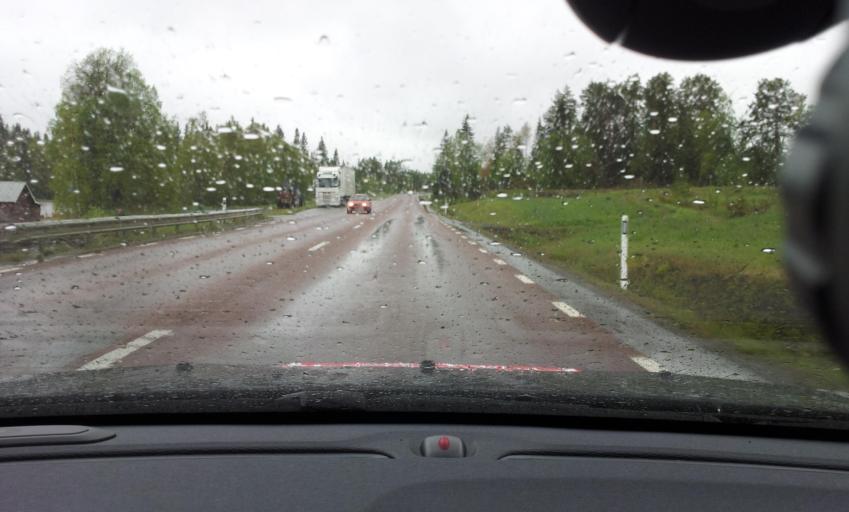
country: SE
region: Jaemtland
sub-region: Bergs Kommun
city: Hoverberg
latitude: 62.9625
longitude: 14.5548
